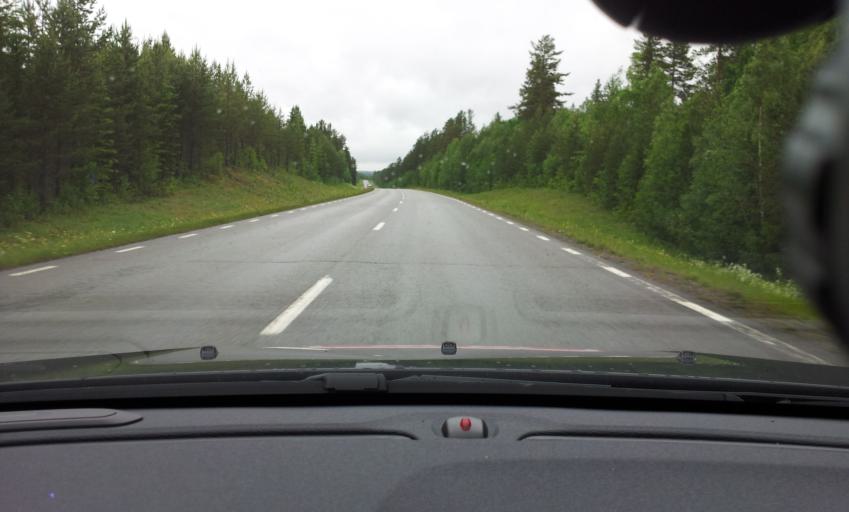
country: SE
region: Jaemtland
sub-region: Krokoms Kommun
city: Krokom
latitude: 63.4352
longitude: 14.4986
